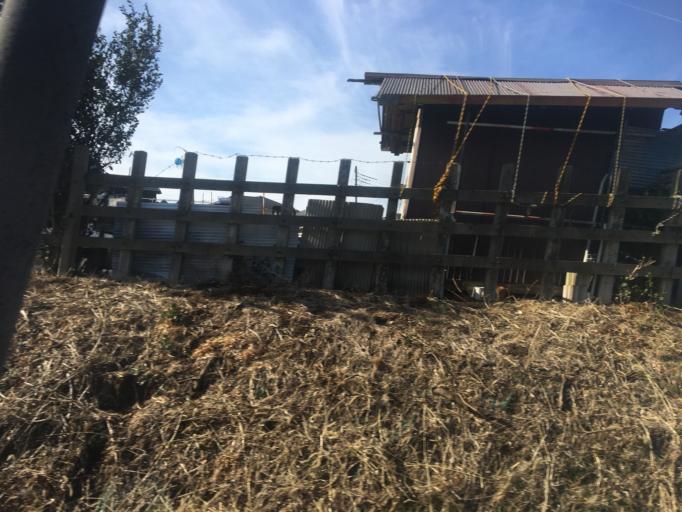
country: JP
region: Saitama
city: Sakado
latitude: 35.9314
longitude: 139.4326
